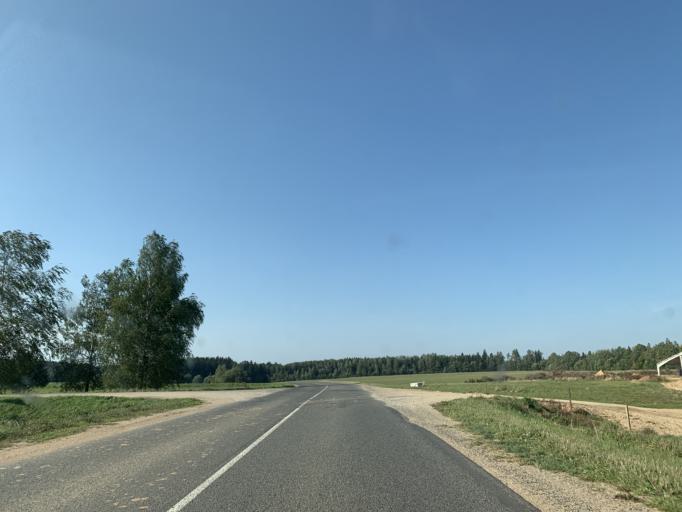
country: BY
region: Minsk
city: Rakaw
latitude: 53.8814
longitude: 26.9625
